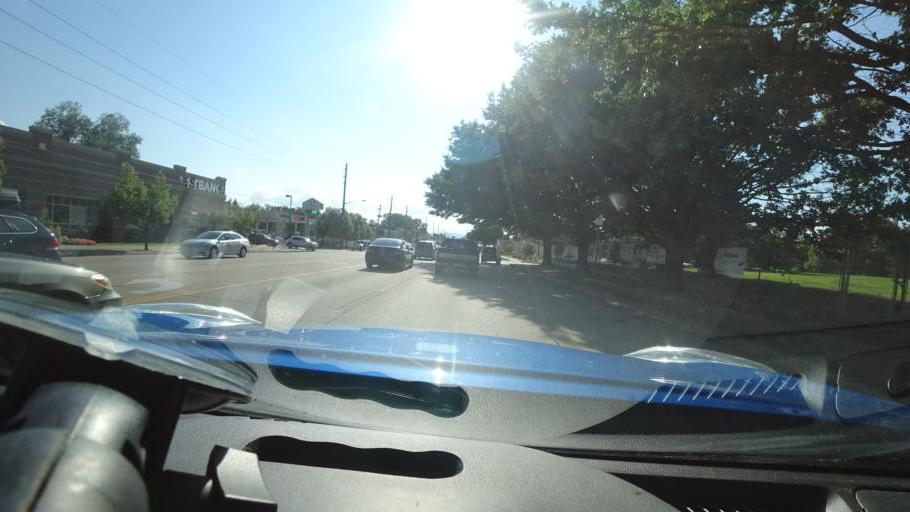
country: US
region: Colorado
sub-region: Arapahoe County
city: Englewood
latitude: 39.6786
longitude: -104.9716
